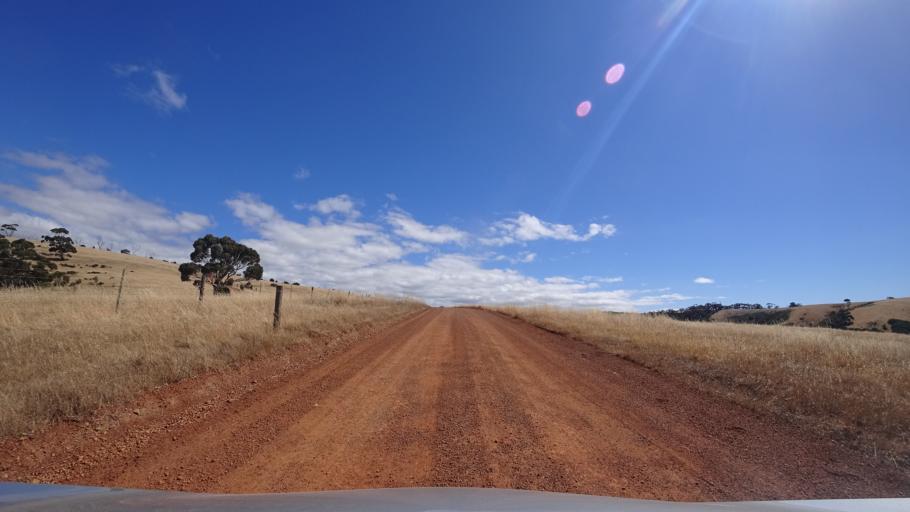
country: AU
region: South Australia
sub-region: Kangaroo Island
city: Kingscote
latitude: -35.6843
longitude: 136.9758
